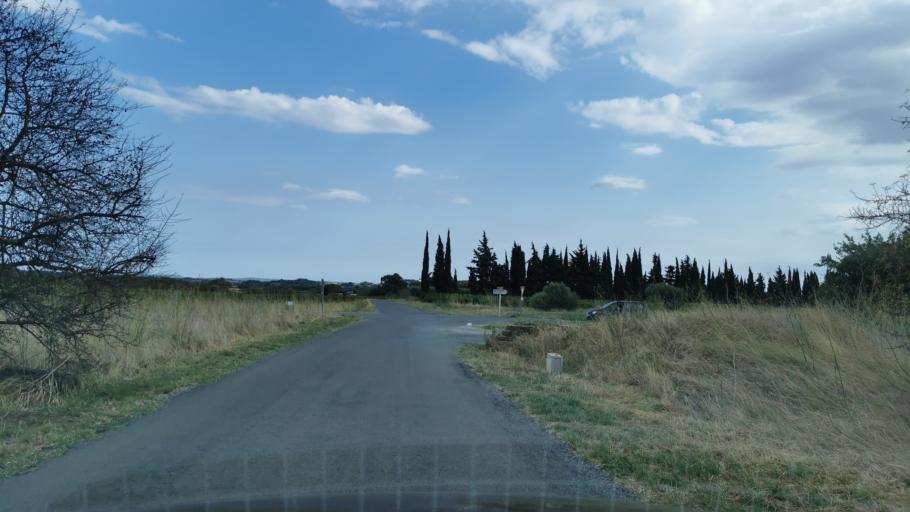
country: FR
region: Languedoc-Roussillon
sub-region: Departement de l'Aude
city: Saint-Marcel-sur-Aude
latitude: 43.2604
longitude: 2.9148
